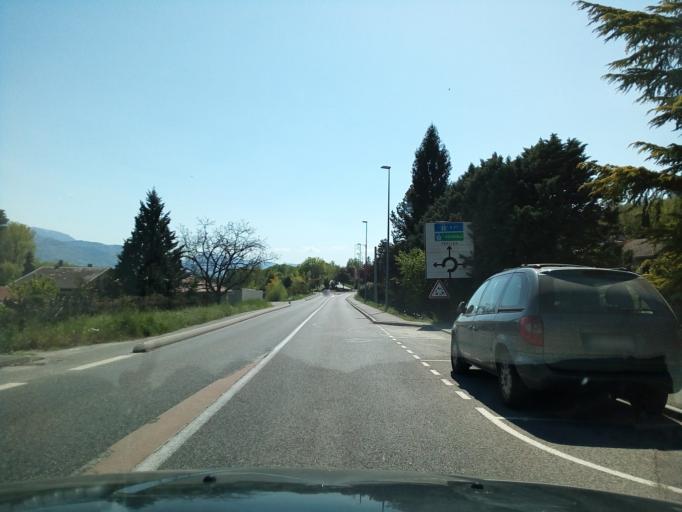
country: FR
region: Rhone-Alpes
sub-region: Departement de l'Isere
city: Saint-Hilaire
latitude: 45.2976
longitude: 5.8984
